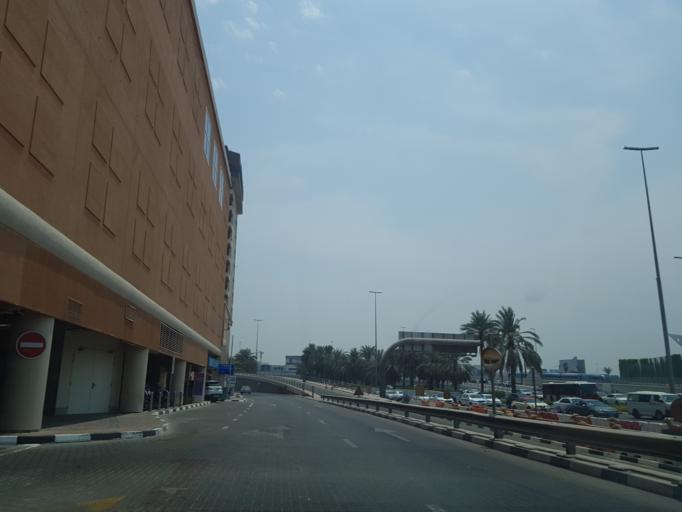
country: AE
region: Ash Shariqah
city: Sharjah
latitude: 25.2504
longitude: 55.3330
